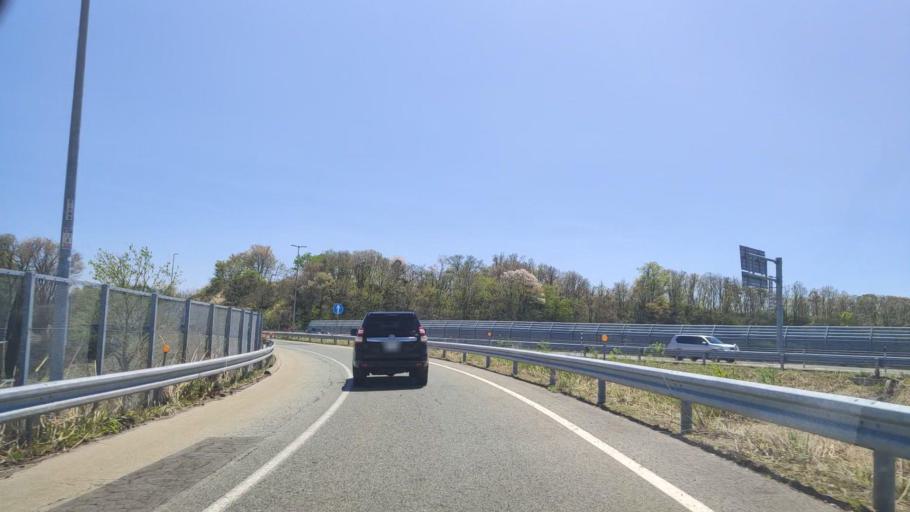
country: JP
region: Yamagata
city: Shinjo
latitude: 38.7380
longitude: 140.2999
